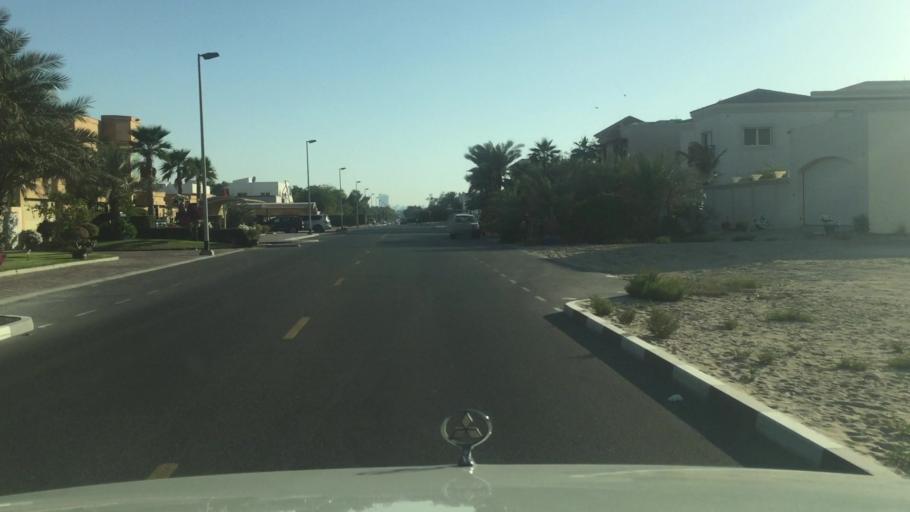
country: AE
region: Dubai
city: Dubai
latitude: 25.1630
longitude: 55.2266
